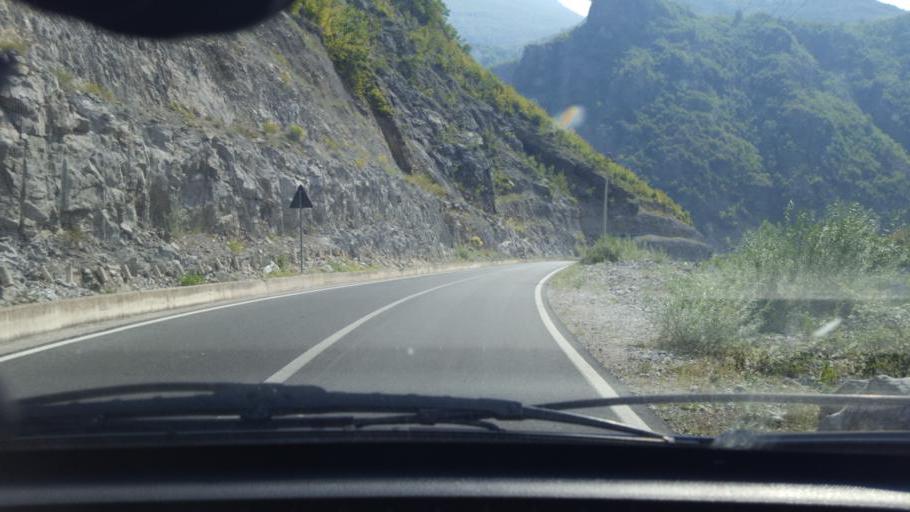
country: AL
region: Shkoder
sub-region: Rrethi i Malesia e Madhe
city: Kastrat
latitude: 42.4582
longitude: 19.5611
